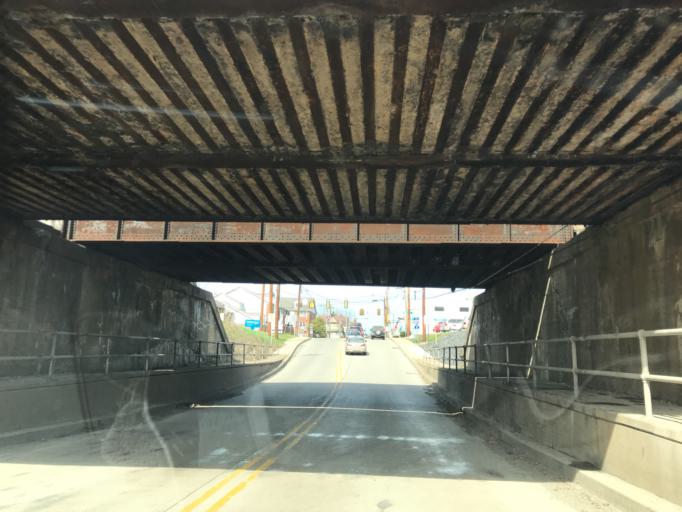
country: US
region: Pennsylvania
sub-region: Northumberland County
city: Northumberland
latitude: 40.8862
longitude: -76.7955
